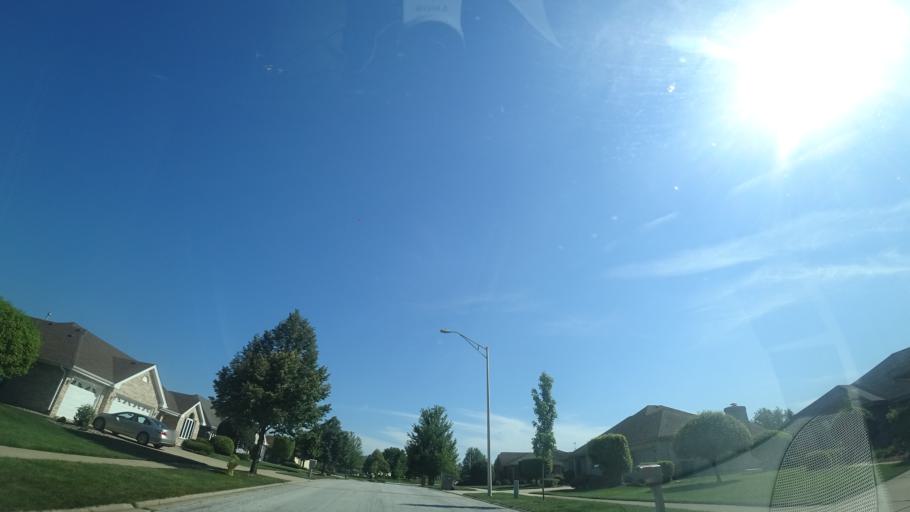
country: US
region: Illinois
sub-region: Will County
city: Mokena
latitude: 41.5694
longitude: -87.8852
